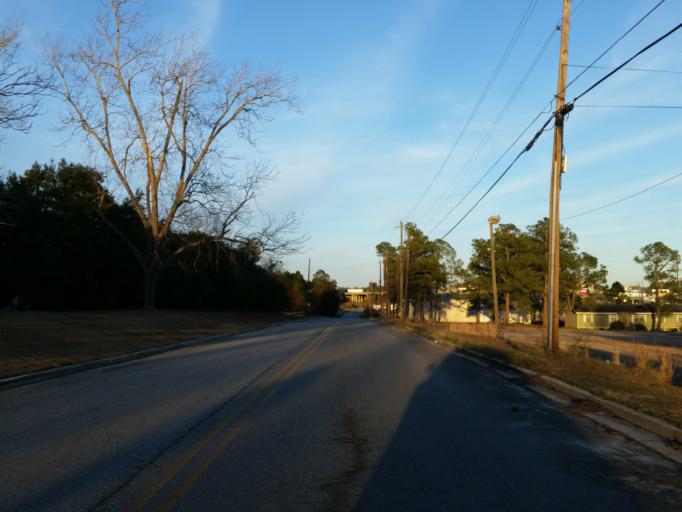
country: US
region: Georgia
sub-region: Tift County
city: Tifton
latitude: 31.4496
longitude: -83.5373
